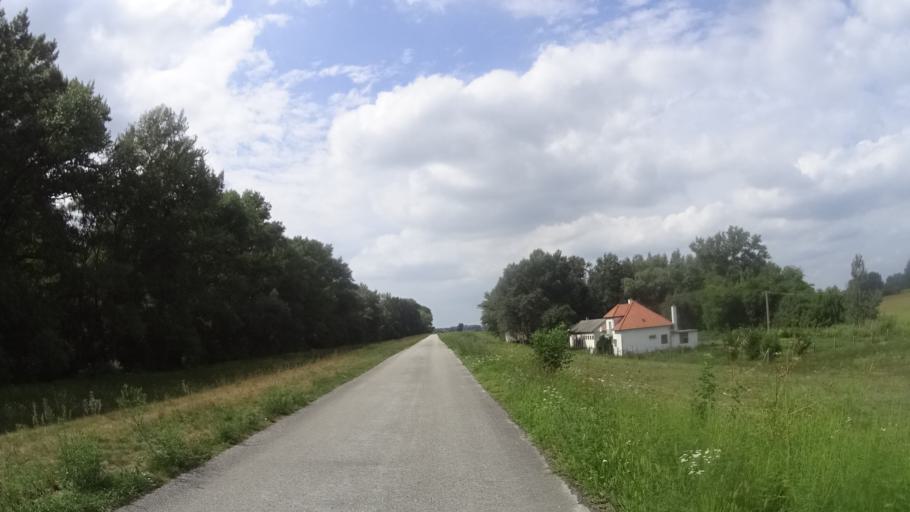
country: SK
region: Trnavsky
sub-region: Okres Dunajska Streda
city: Velky Meder
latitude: 47.7914
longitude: 17.6892
